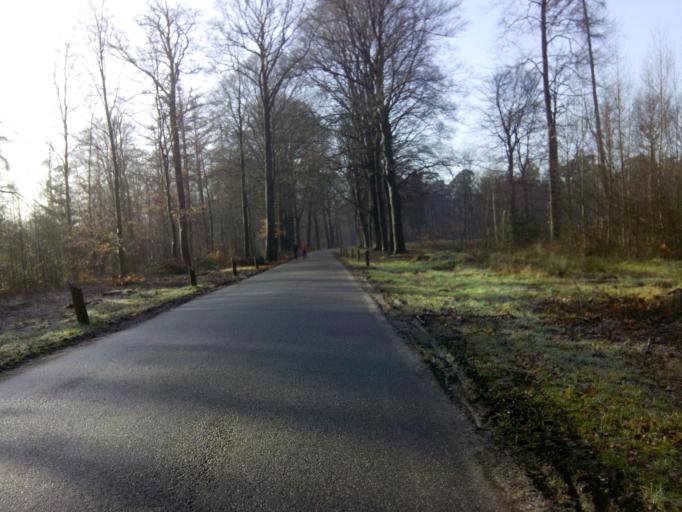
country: NL
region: Utrecht
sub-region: Gemeente Amersfoort
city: Randenbroek
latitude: 52.1119
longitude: 5.3932
